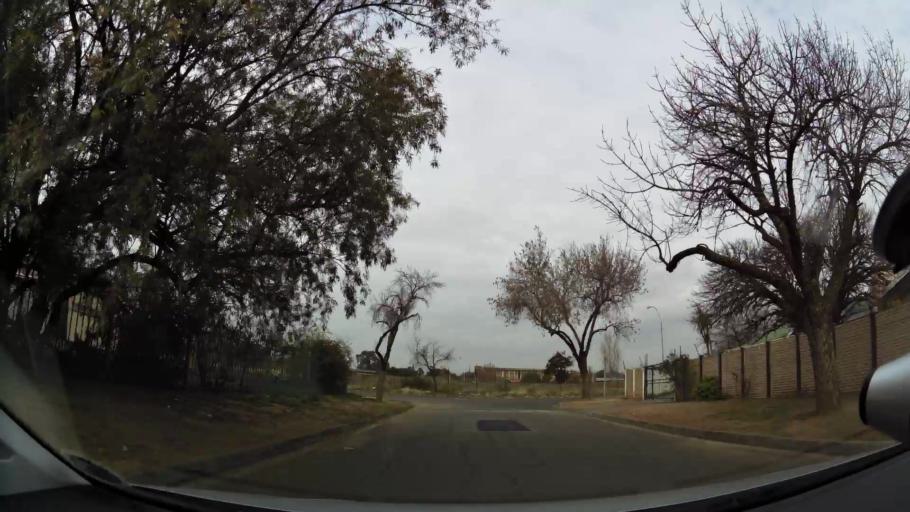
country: ZA
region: Orange Free State
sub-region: Mangaung Metropolitan Municipality
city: Bloemfontein
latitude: -29.1229
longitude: 26.1929
